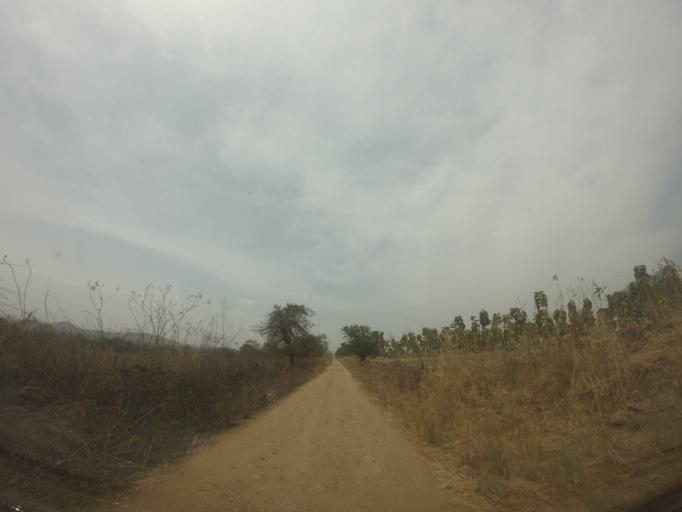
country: UG
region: Northern Region
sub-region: Nebbi District
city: Nebbi
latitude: 2.6353
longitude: 31.0304
